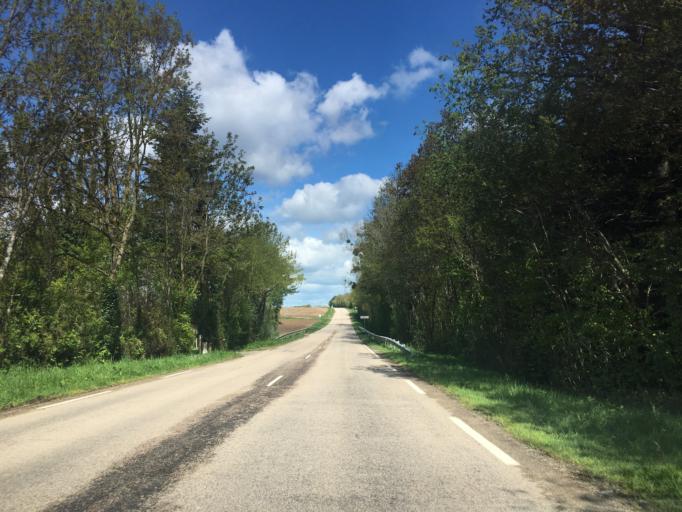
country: FR
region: Lower Normandy
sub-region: Departement de l'Orne
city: Rai
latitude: 48.8029
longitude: 0.5868
